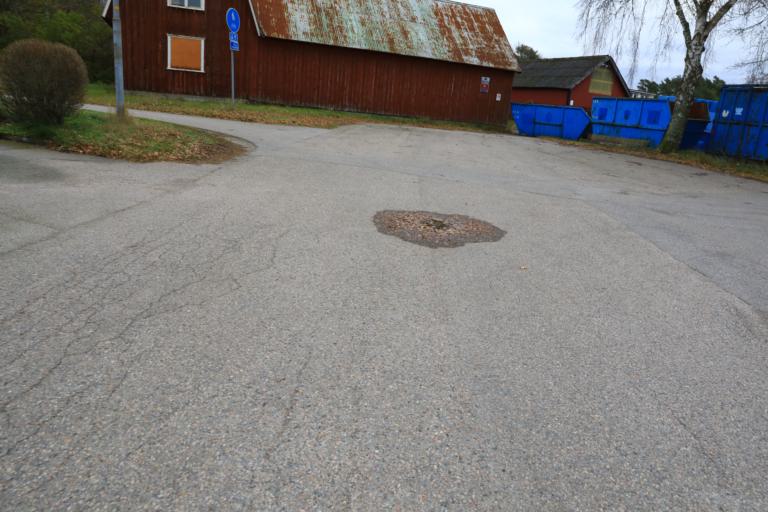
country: SE
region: Halland
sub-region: Varbergs Kommun
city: Tvaaker
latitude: 57.0397
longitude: 12.3994
